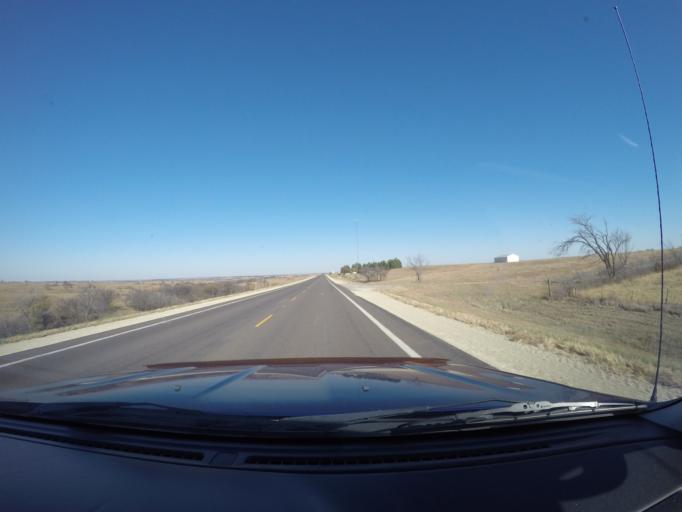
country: US
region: Kansas
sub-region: Marshall County
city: Blue Rapids
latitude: 39.6751
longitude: -96.7508
